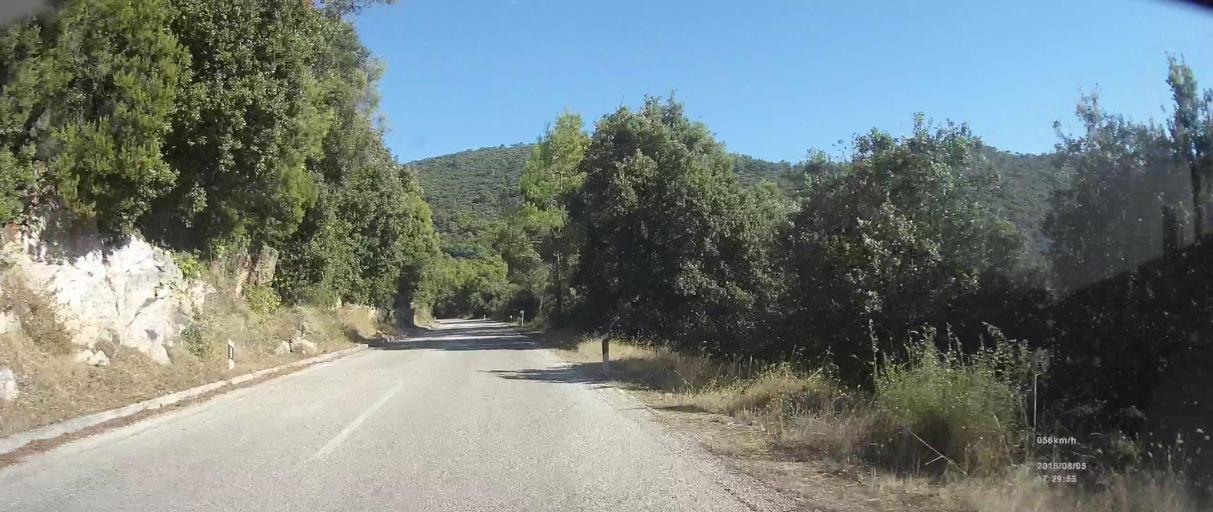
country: HR
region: Dubrovacko-Neretvanska
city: Blato
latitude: 42.7766
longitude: 17.4119
